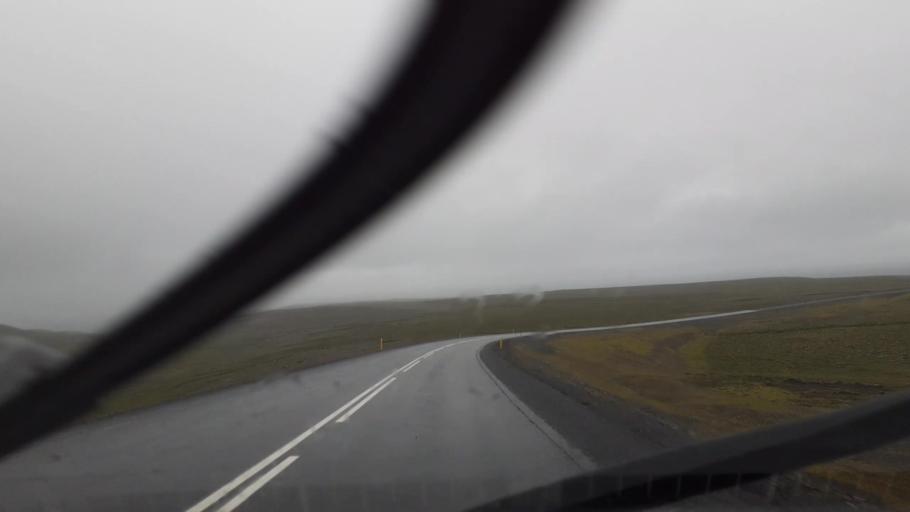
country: IS
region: Northeast
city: Husavik
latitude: 66.2376
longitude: -15.7583
